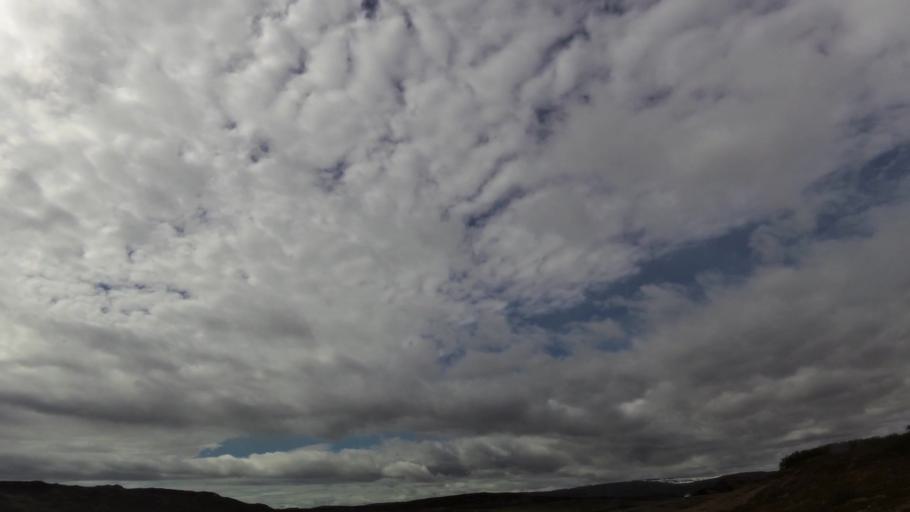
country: IS
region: West
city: Stykkisholmur
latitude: 65.5353
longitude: -22.0923
